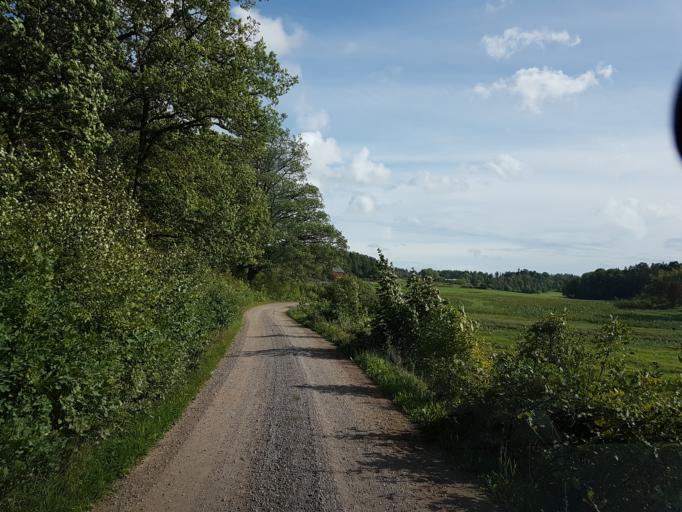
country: SE
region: OEstergoetland
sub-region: Linkopings Kommun
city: Sturefors
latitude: 58.3066
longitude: 15.8537
